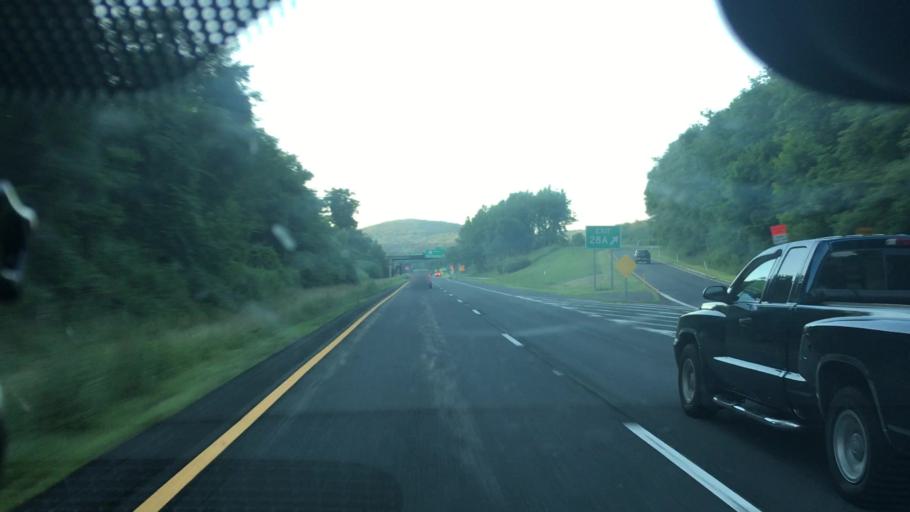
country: US
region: Massachusetts
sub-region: Franklin County
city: Bernardston
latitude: 42.6682
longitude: -72.5433
